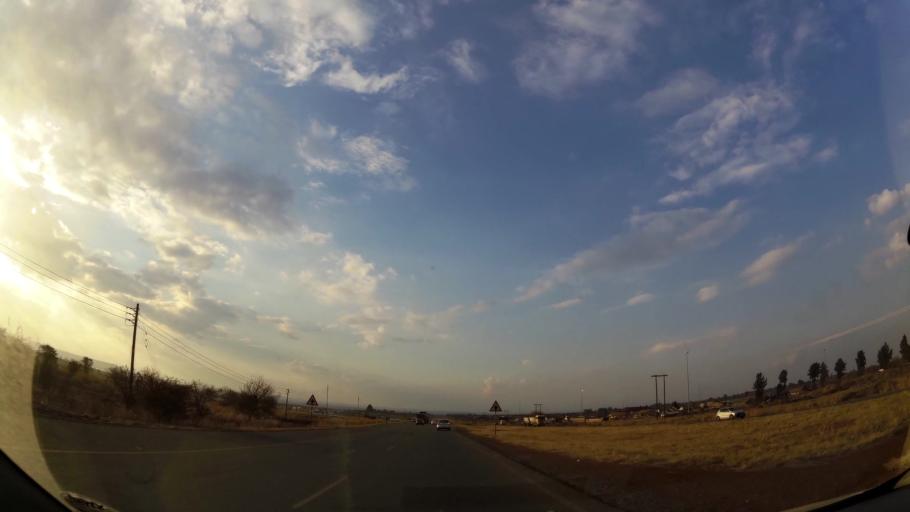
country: ZA
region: Gauteng
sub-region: City of Johannesburg Metropolitan Municipality
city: Orange Farm
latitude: -26.5928
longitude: 27.8206
